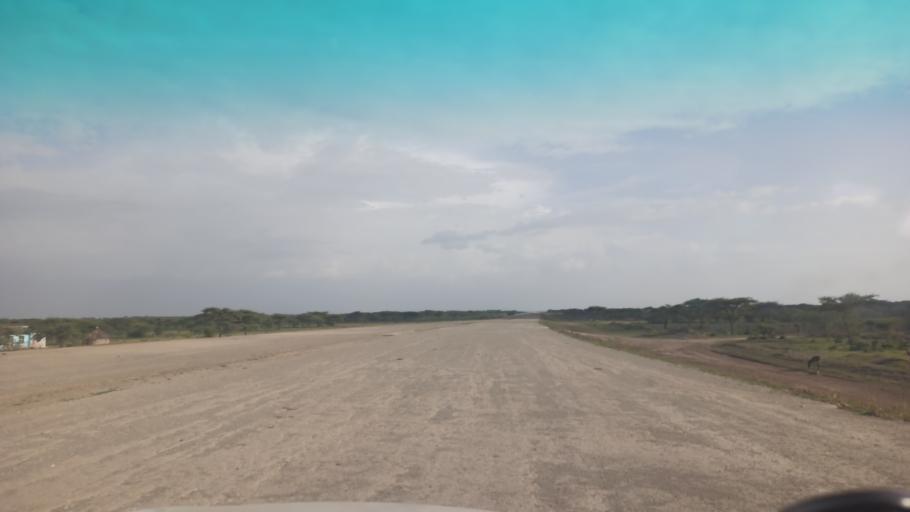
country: ET
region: Oromiya
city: Ziway
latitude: 7.6615
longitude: 38.6838
